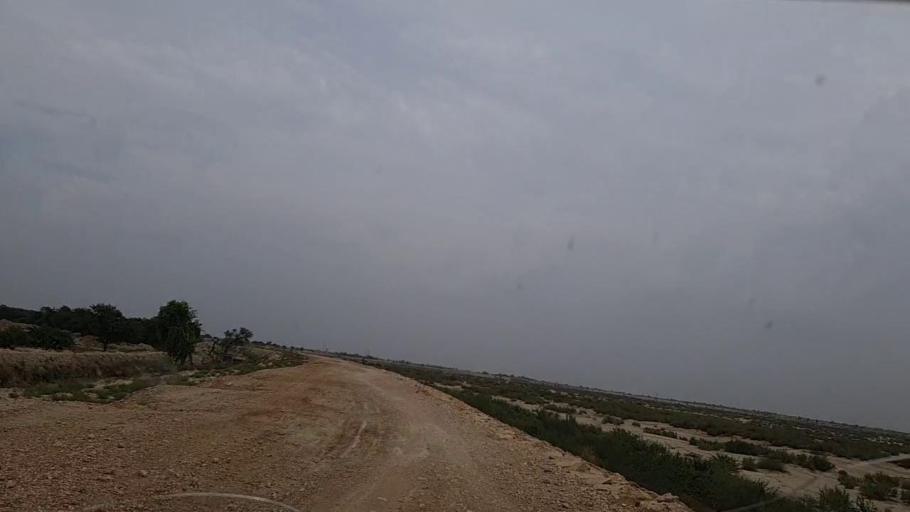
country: PK
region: Sindh
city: Johi
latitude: 26.7075
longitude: 67.5885
